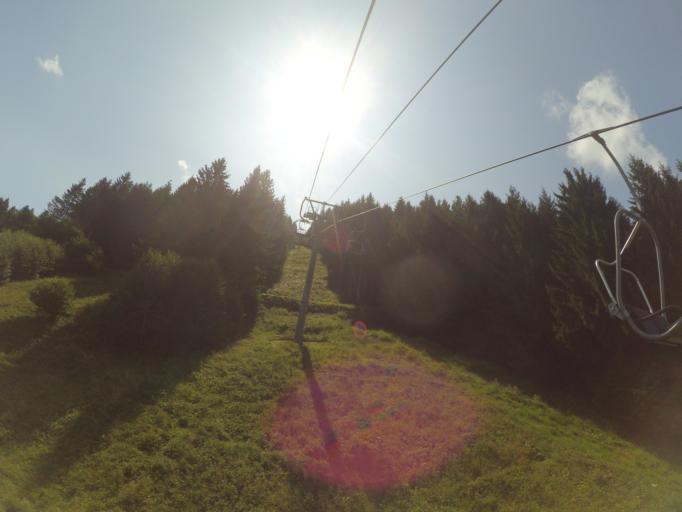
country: DE
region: Bavaria
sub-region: Swabia
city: Halblech
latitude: 47.6101
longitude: 10.8088
